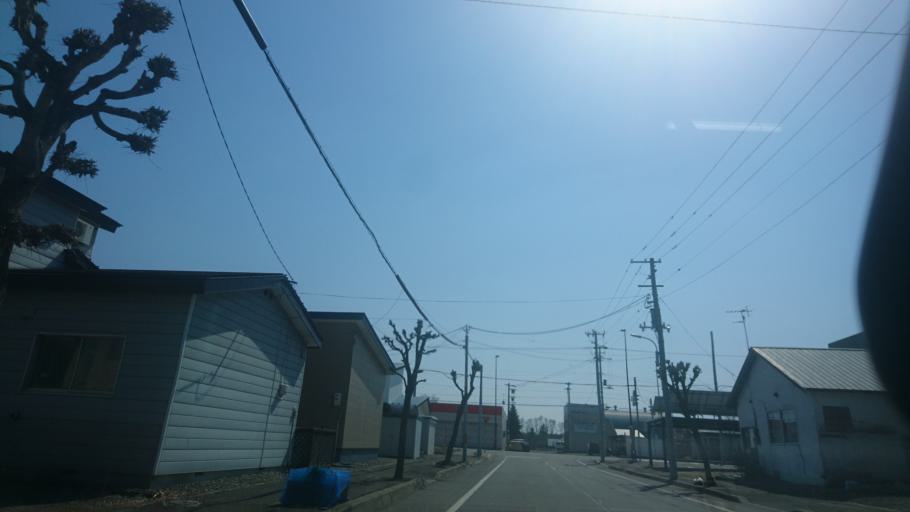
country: JP
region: Hokkaido
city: Obihiro
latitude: 42.9120
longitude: 143.0565
